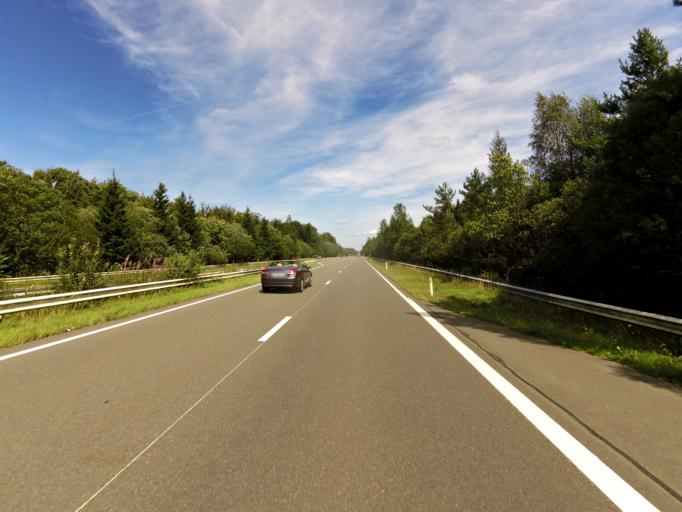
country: BE
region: Wallonia
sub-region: Province du Luxembourg
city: Saint-Hubert
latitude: 50.0632
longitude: 5.4151
